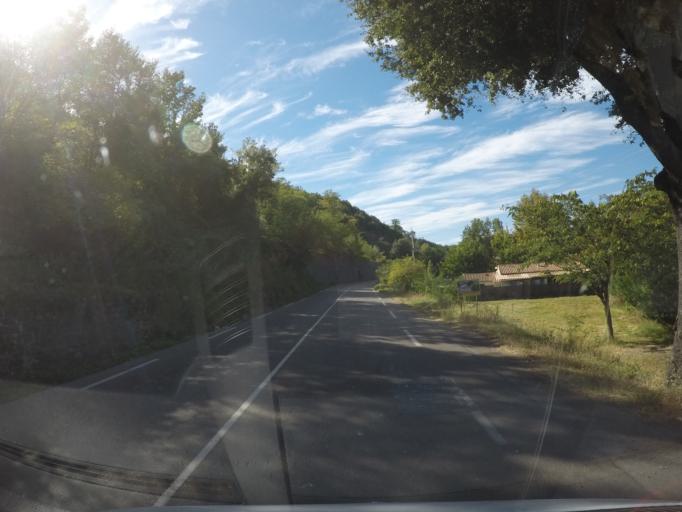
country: FR
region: Languedoc-Roussillon
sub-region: Departement du Gard
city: Boisset-et-Gaujac
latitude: 44.0384
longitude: 3.9942
